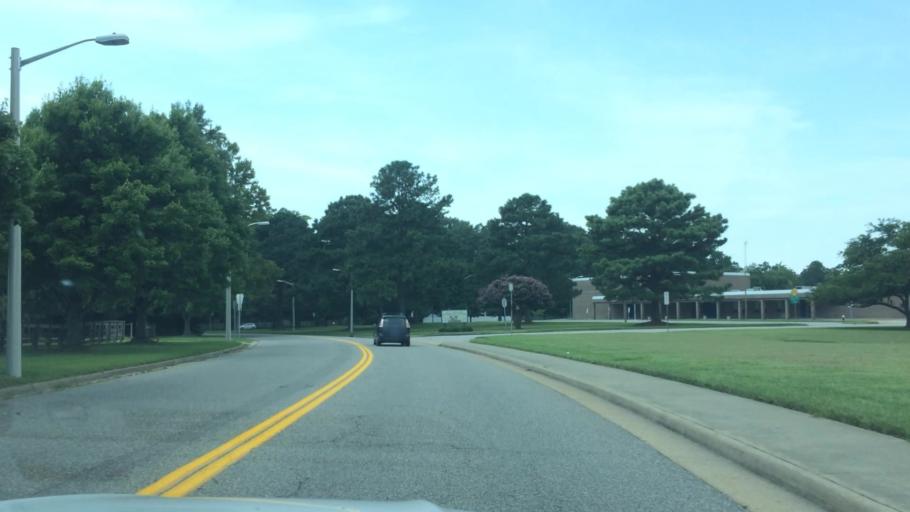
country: US
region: Virginia
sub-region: Isle of Wight County
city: Rushmere
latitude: 37.0940
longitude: -76.5327
